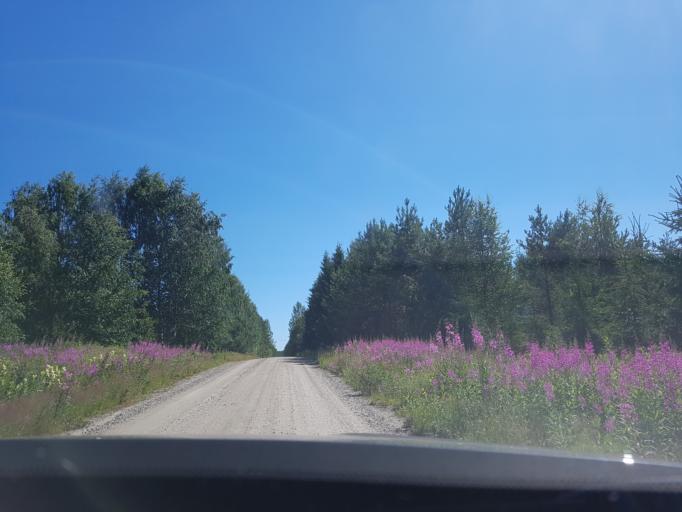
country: FI
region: Kainuu
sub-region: Kehys-Kainuu
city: Kuhmo
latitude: 64.1847
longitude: 29.5789
